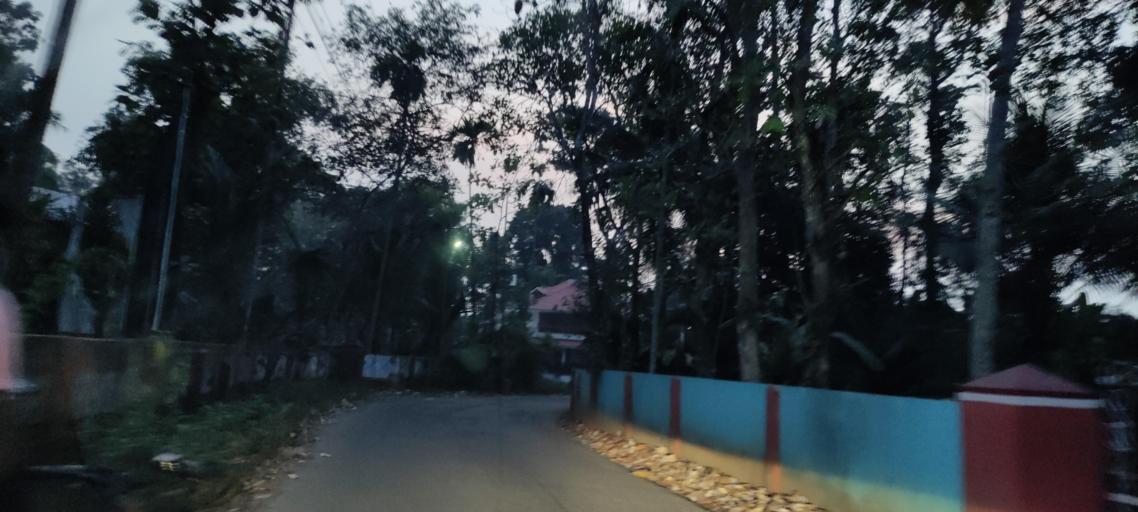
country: IN
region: Kerala
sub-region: Alappuzha
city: Mavelikara
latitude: 9.3215
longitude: 76.4591
